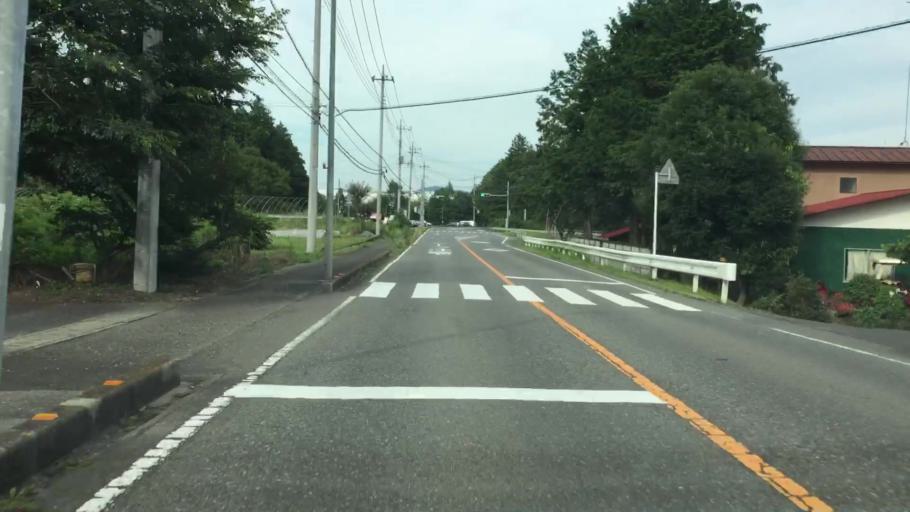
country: JP
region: Tochigi
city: Imaichi
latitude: 36.7442
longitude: 139.7436
